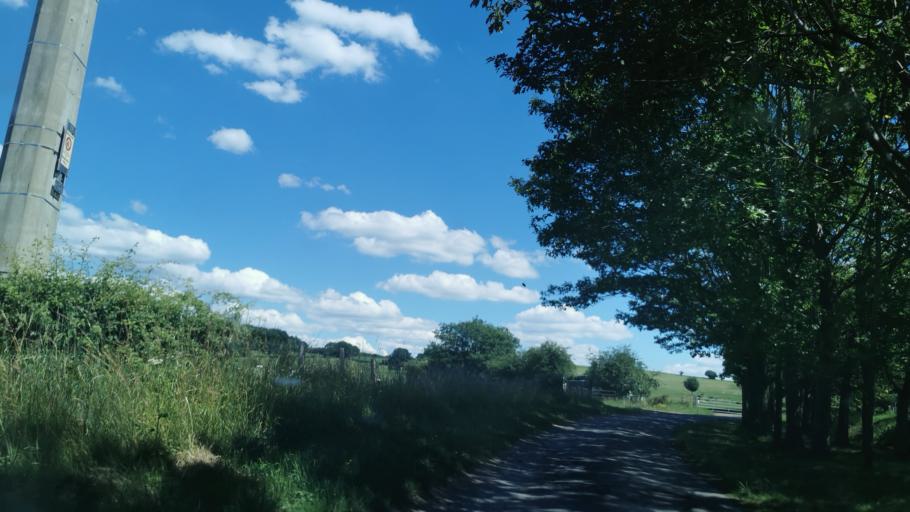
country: BE
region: Wallonia
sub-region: Province de Liege
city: Theux
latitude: 50.5430
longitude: 5.8364
